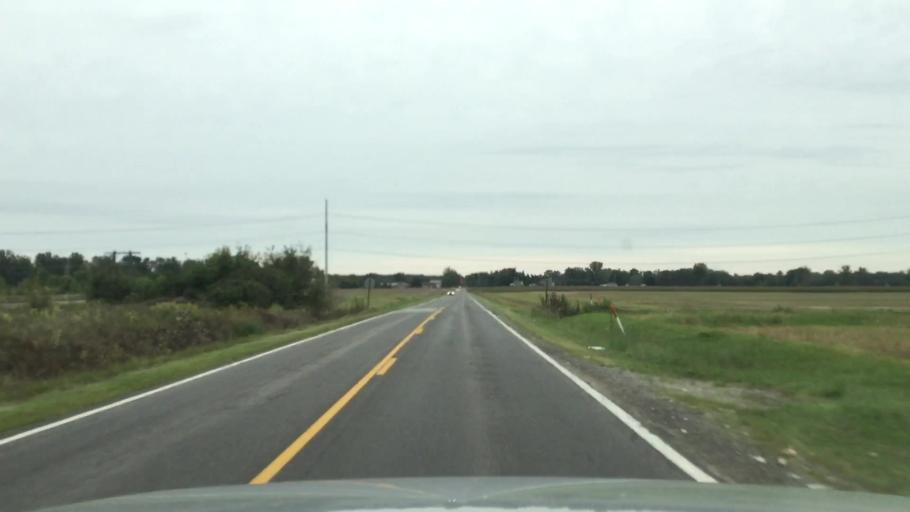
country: US
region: Michigan
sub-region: Washtenaw County
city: Milan
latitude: 42.1164
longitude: -83.6961
